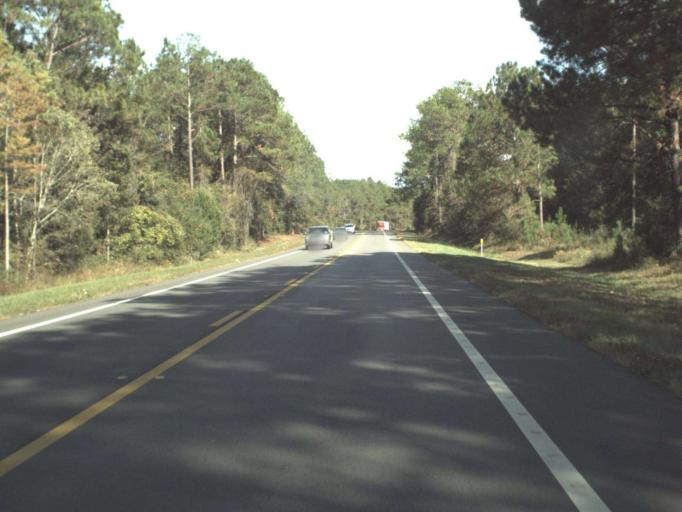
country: US
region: Florida
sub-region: Holmes County
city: Bonifay
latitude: 30.7796
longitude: -85.7933
